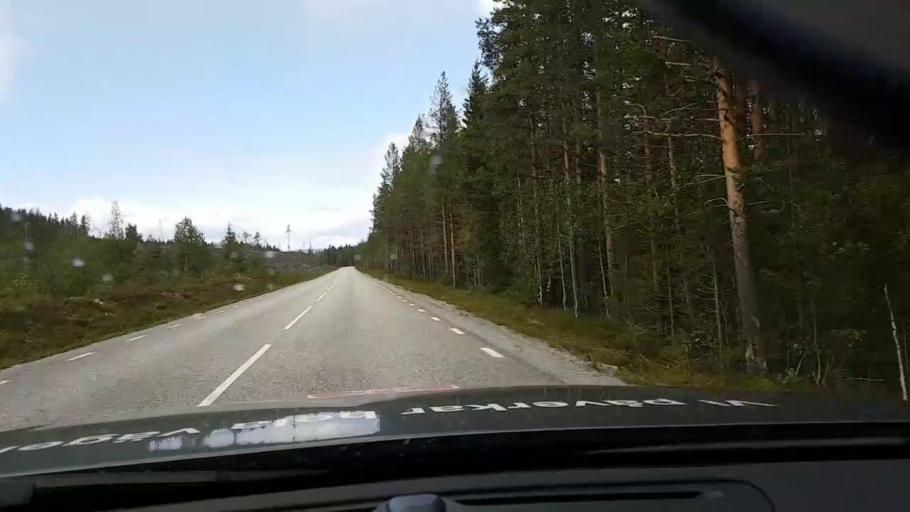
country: SE
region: Vaesternorrland
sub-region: OErnskoeldsviks Kommun
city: Bredbyn
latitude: 63.7053
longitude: 17.7610
